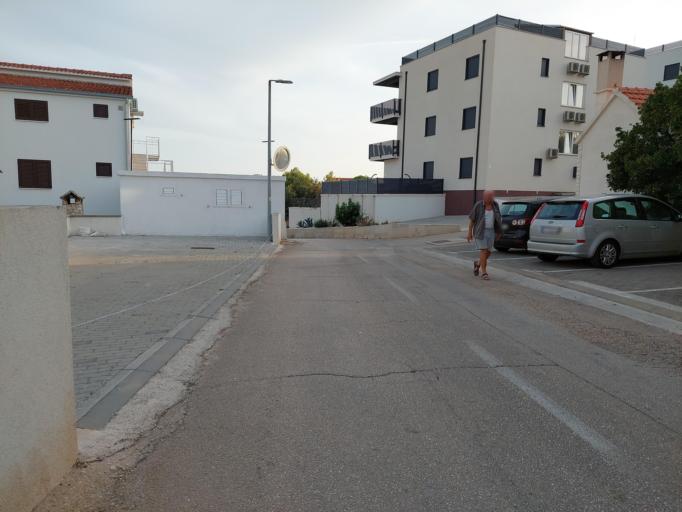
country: HR
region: Splitsko-Dalmatinska
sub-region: Grad Trogir
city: Trogir
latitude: 43.4946
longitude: 16.2707
